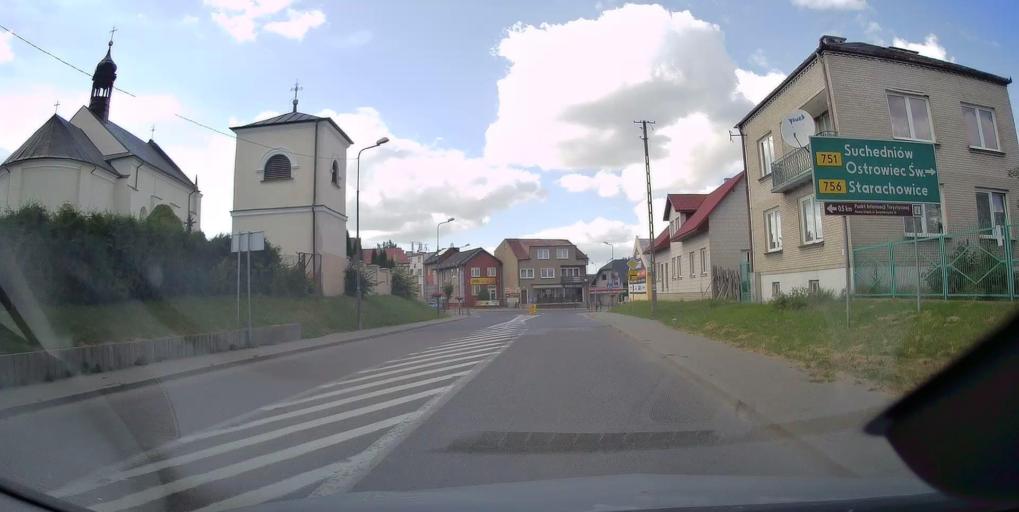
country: PL
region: Swietokrzyskie
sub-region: Powiat kielecki
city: Nowa Slupia
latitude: 50.8632
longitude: 21.0903
